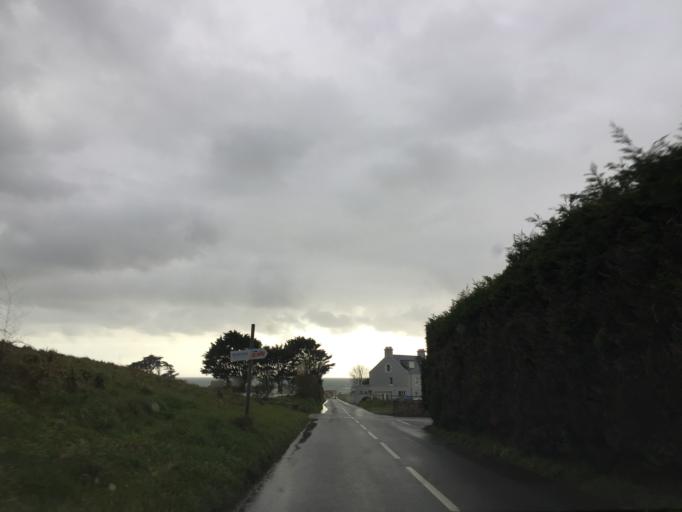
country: JE
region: St Helier
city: Saint Helier
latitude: 49.2335
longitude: -2.2320
